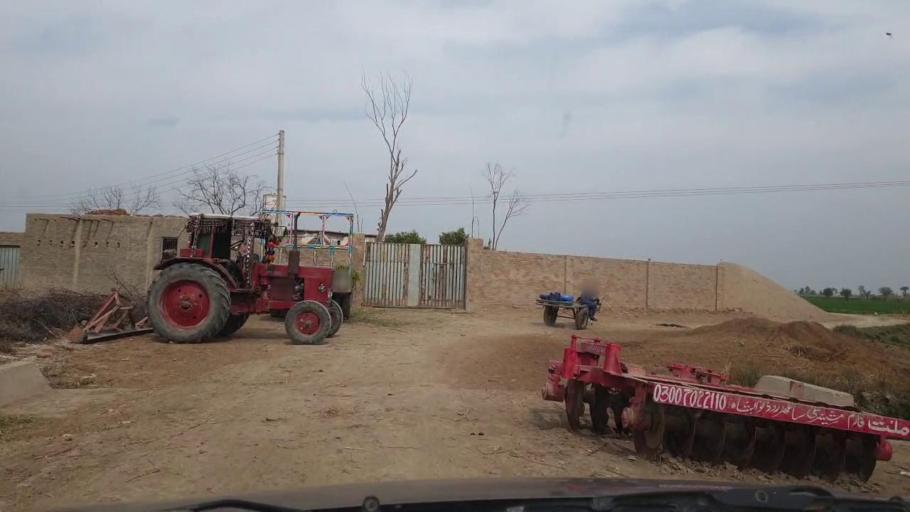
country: PK
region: Sindh
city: Sinjhoro
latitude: 26.0731
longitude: 68.8324
